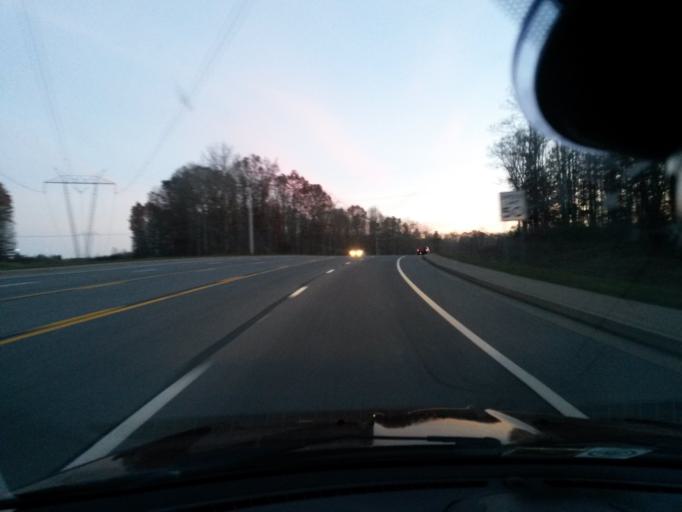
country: US
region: West Virginia
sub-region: Raleigh County
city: Stanaford
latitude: 37.7853
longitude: -81.1520
